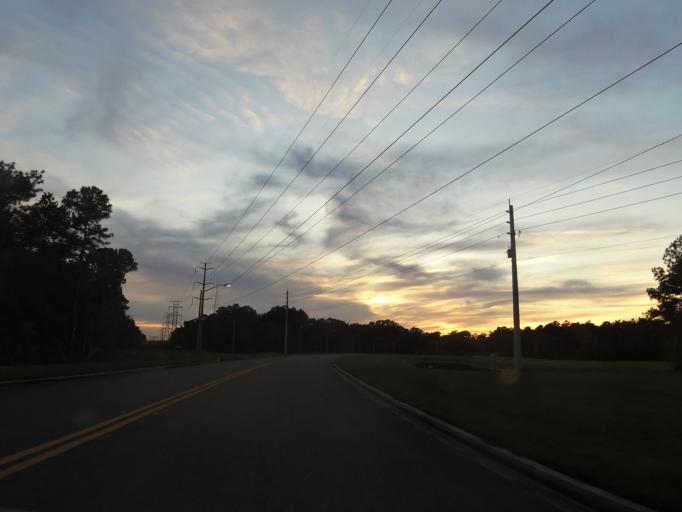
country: US
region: Florida
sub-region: Saint Johns County
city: Fruit Cove
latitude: 30.1534
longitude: -81.5216
